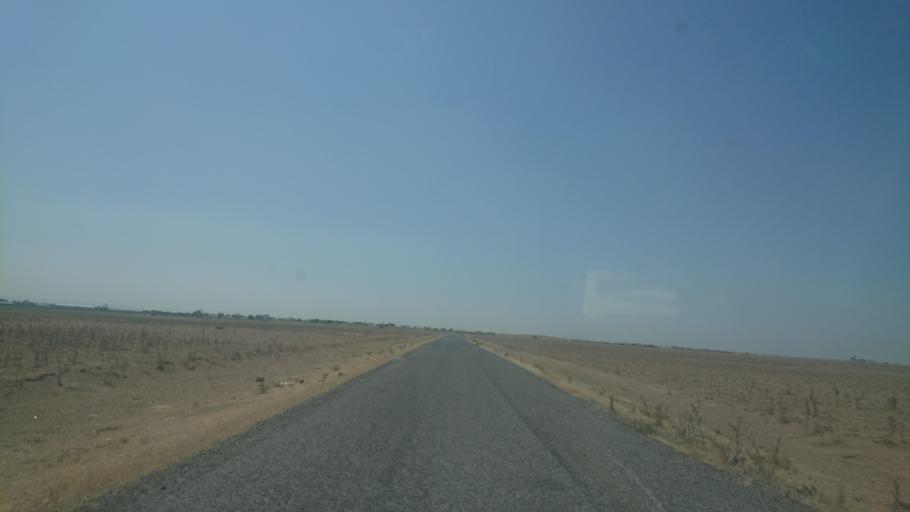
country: TR
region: Aksaray
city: Yesilova
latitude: 38.3038
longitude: 33.7330
